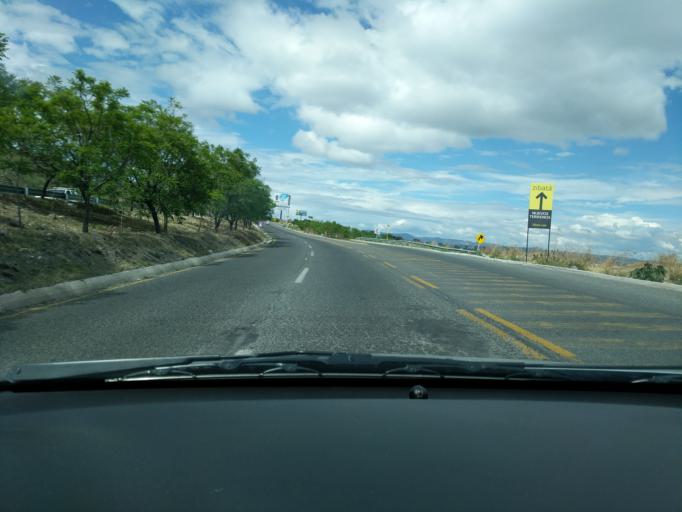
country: MX
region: Queretaro
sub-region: El Marques
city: La Pradera
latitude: 20.6628
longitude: -100.3315
